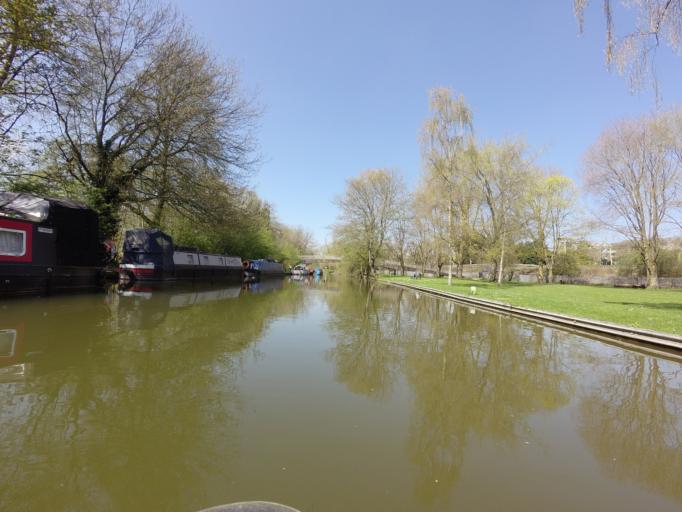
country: GB
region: England
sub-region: Hertfordshire
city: Berkhamsted
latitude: 51.7640
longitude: -0.5697
